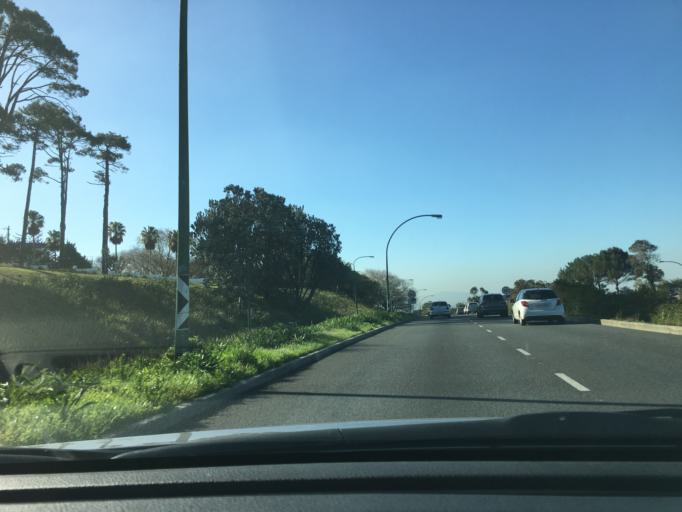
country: ZA
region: Western Cape
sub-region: City of Cape Town
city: Newlands
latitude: -33.9960
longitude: 18.4534
